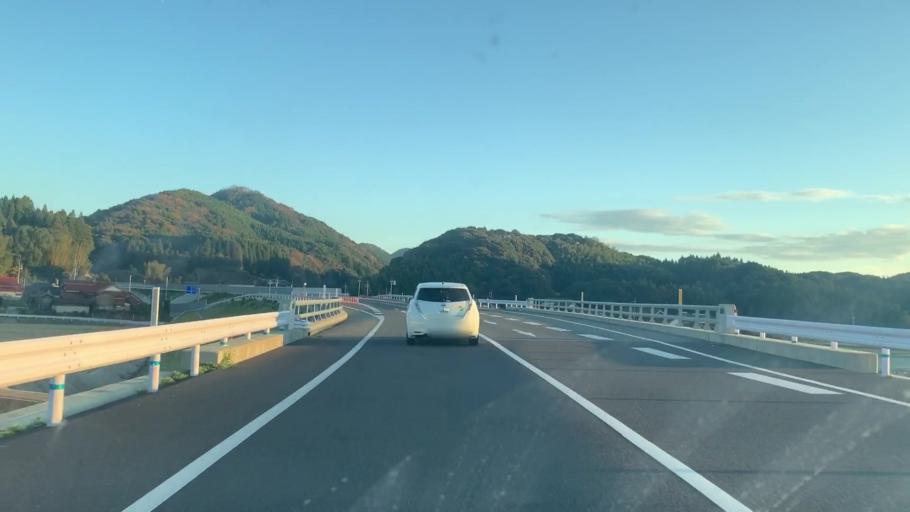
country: JP
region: Saga Prefecture
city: Takeocho-takeo
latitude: 33.2597
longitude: 129.9730
